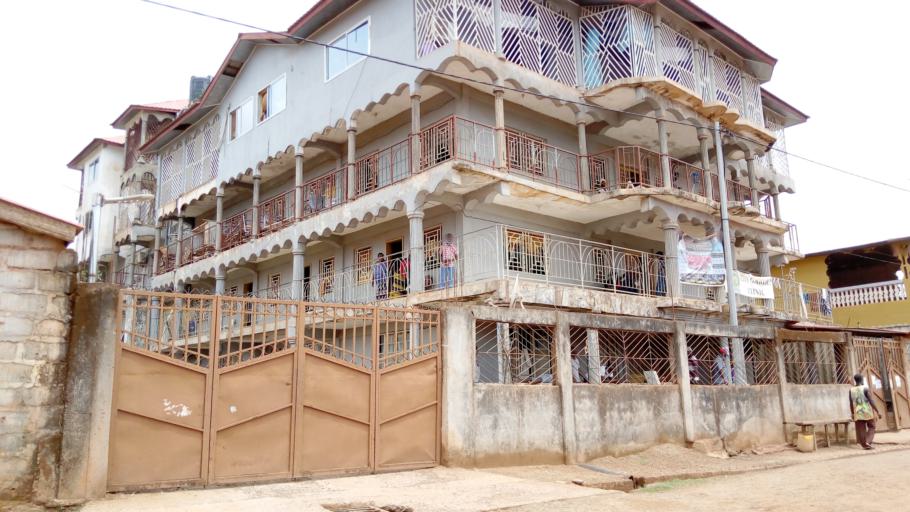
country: SL
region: Northern Province
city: Makeni
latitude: 8.8887
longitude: -12.0354
